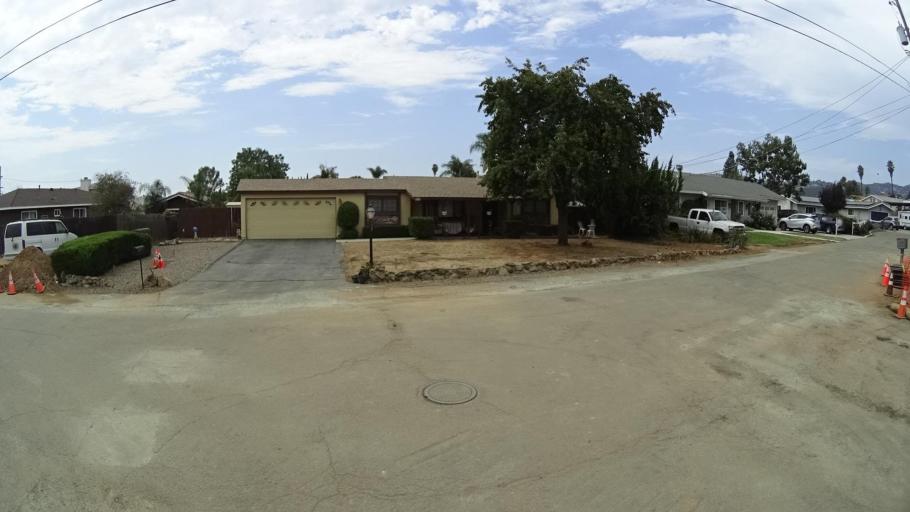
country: US
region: California
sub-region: San Diego County
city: Escondido
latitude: 33.1485
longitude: -117.1209
